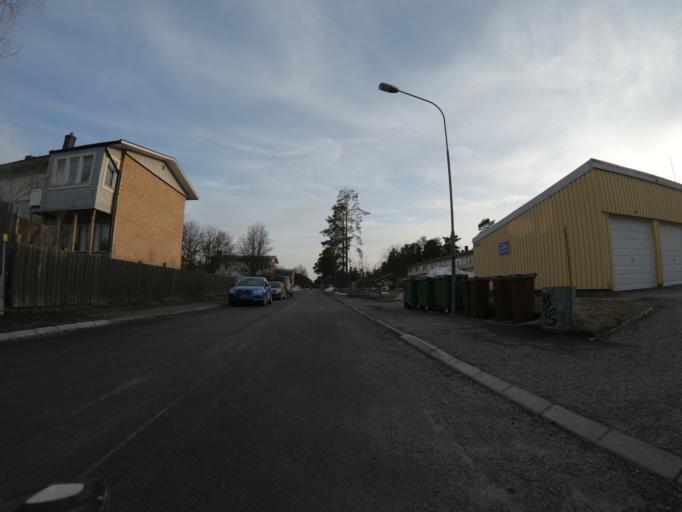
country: SE
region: Vaesterbotten
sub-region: Umea Kommun
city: Umea
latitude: 63.8436
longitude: 20.2833
